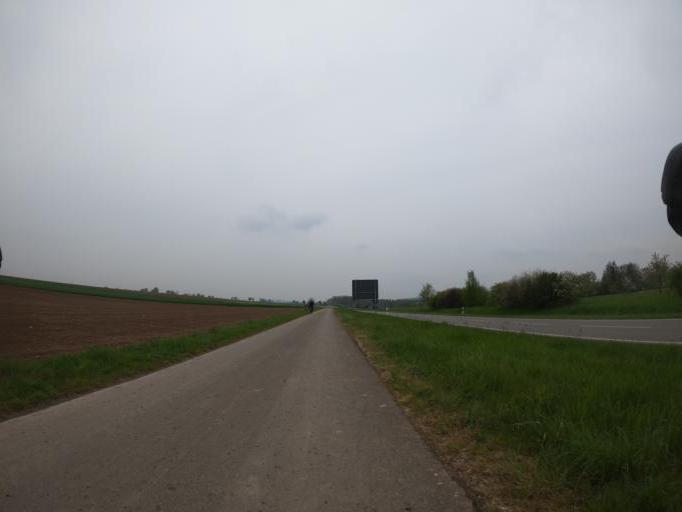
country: DE
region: Baden-Wuerttemberg
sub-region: Regierungsbezirk Stuttgart
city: Sersheim
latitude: 48.9500
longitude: 9.0156
